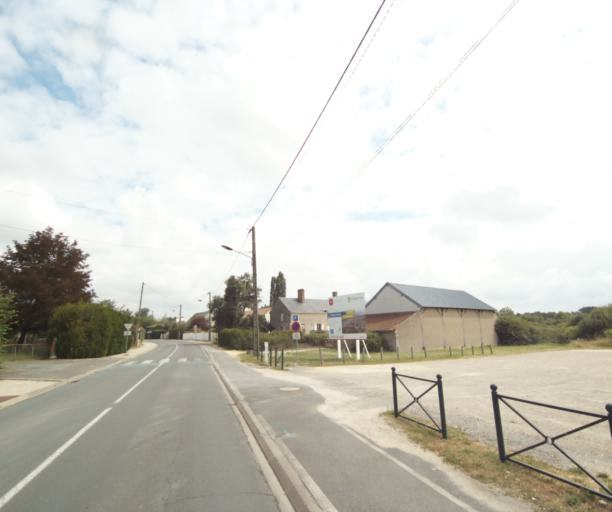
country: FR
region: Centre
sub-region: Departement du Loiret
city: Checy
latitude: 47.9007
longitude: 2.0276
